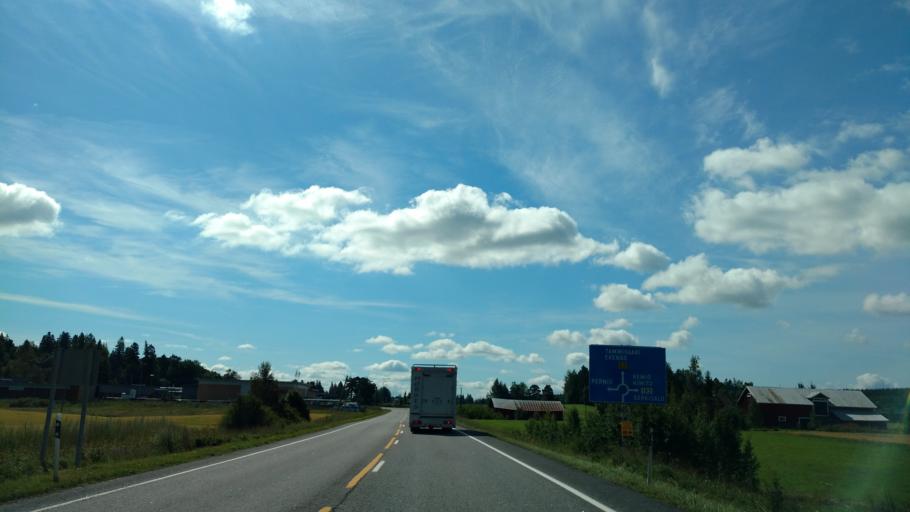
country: FI
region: Varsinais-Suomi
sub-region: Salo
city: Pernioe
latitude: 60.2086
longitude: 23.1107
